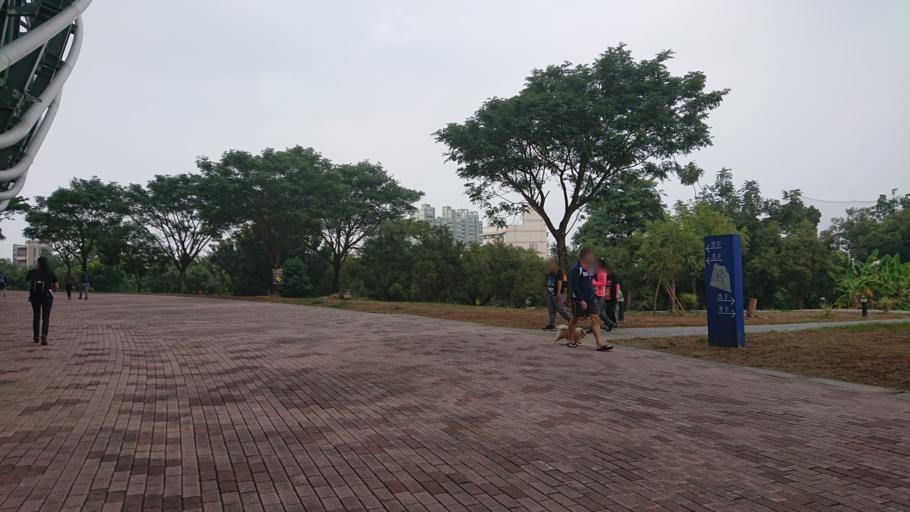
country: TW
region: Kaohsiung
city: Kaohsiung
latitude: 22.7042
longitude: 120.2951
